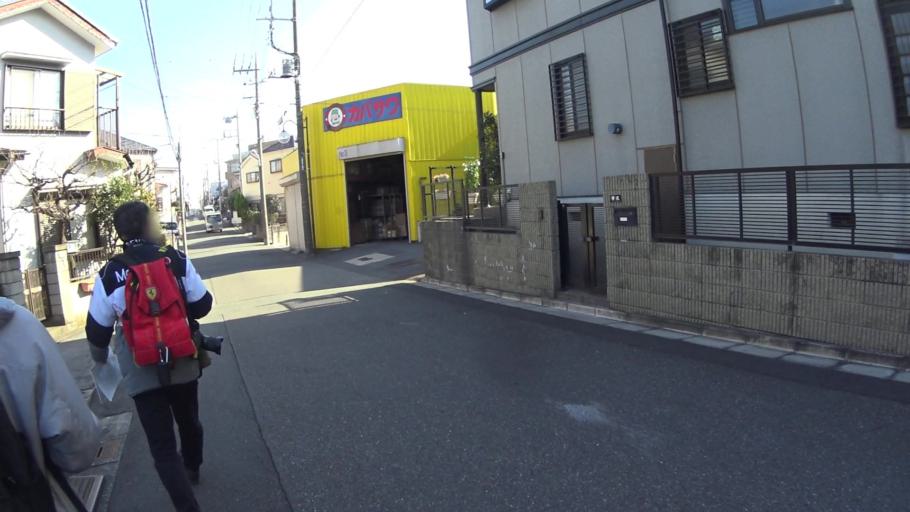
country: JP
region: Saitama
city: Yono
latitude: 35.9034
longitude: 139.6359
